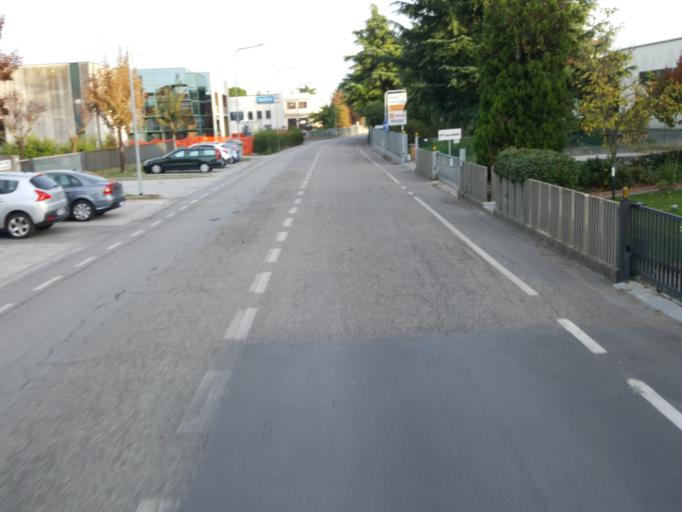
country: IT
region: Emilia-Romagna
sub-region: Provincia di Ravenna
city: Faenza
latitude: 44.3008
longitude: 11.8703
